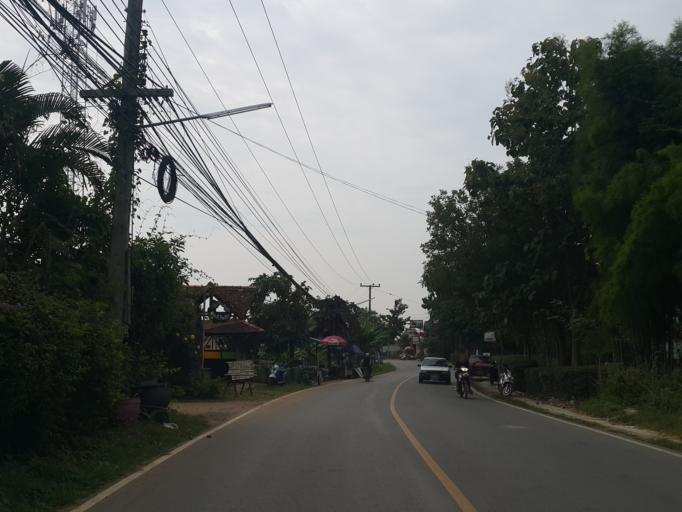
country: TH
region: Chiang Mai
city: Pai
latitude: 19.3662
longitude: 98.4395
